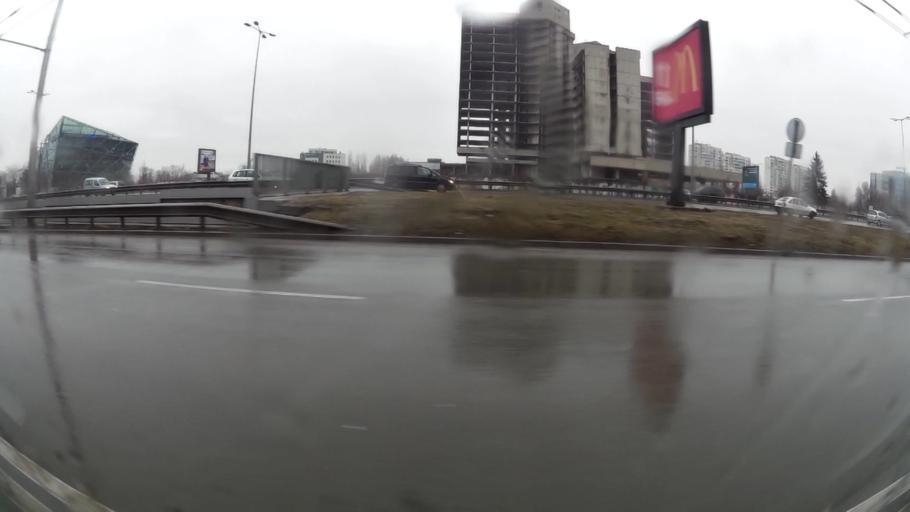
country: BG
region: Sofia-Capital
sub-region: Stolichna Obshtina
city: Sofia
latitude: 42.6634
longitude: 23.3749
